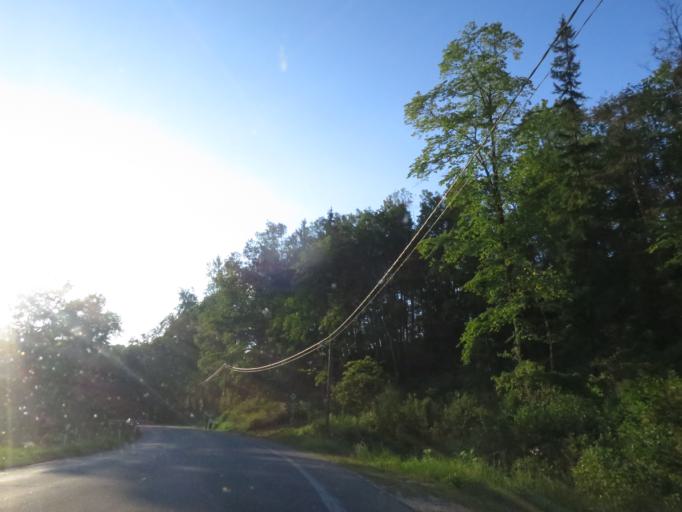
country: LV
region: Sigulda
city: Sigulda
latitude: 57.1660
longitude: 24.8479
